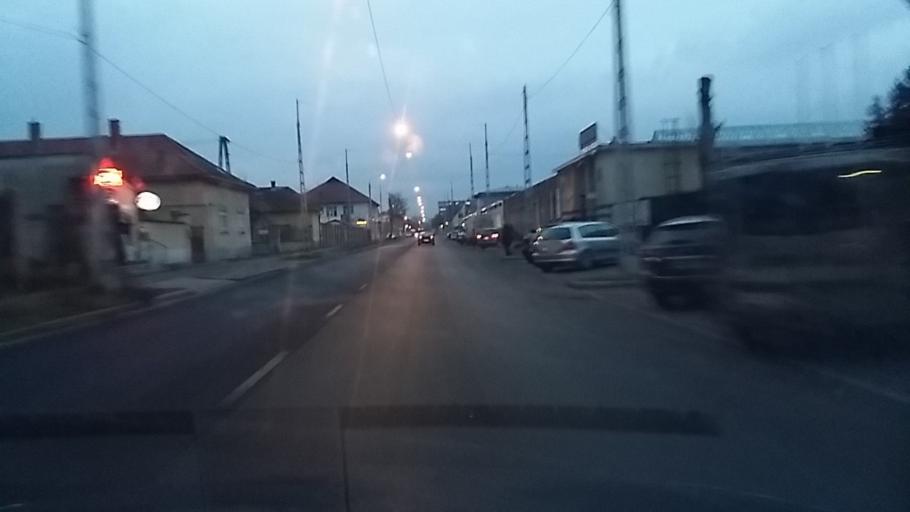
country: HU
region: Budapest
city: Budapest IV. keruelet
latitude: 47.5731
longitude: 19.0888
